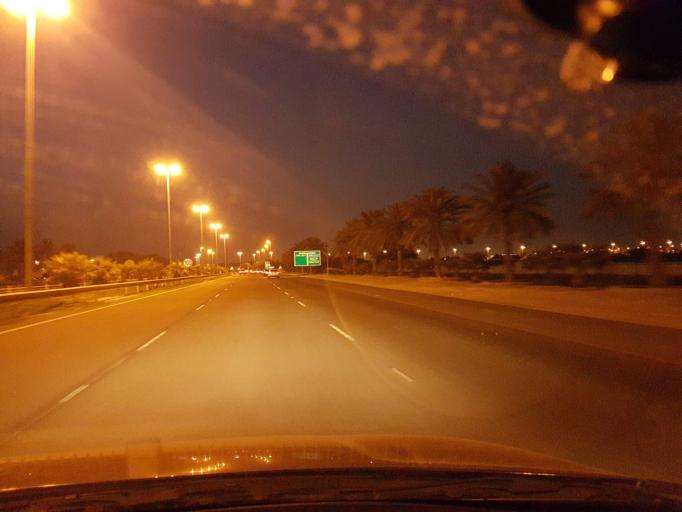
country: BH
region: Central Governorate
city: Dar Kulayb
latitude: 26.0523
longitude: 50.4999
